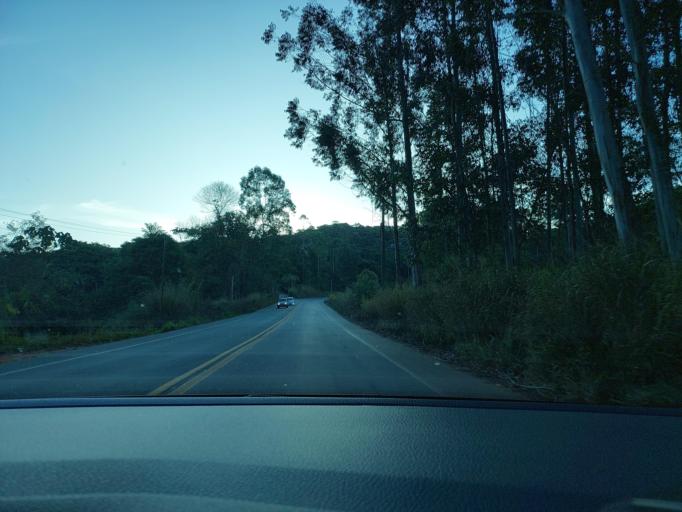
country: BR
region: Minas Gerais
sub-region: Vicosa
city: Vicosa
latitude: -20.8271
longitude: -42.8171
